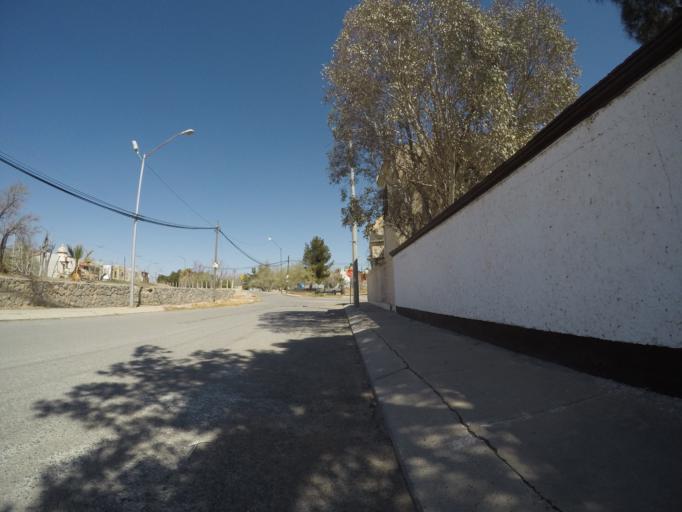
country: MX
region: Chihuahua
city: Ciudad Juarez
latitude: 31.6908
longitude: -106.4174
